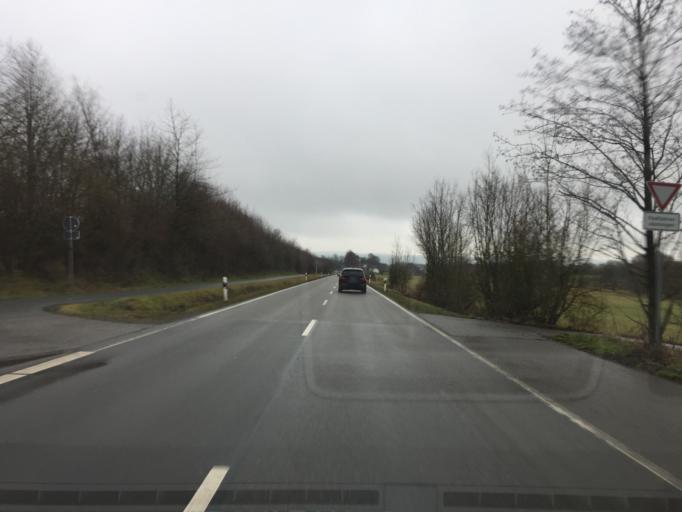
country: DE
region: North Rhine-Westphalia
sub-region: Regierungsbezirk Arnsberg
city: Medebach
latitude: 51.2074
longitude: 8.6771
